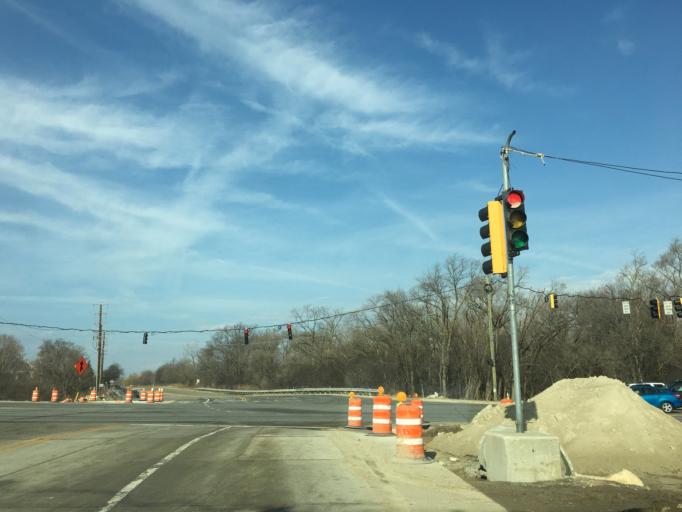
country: US
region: Illinois
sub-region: Cook County
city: Hoffman Estates
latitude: 42.0669
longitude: -88.0783
